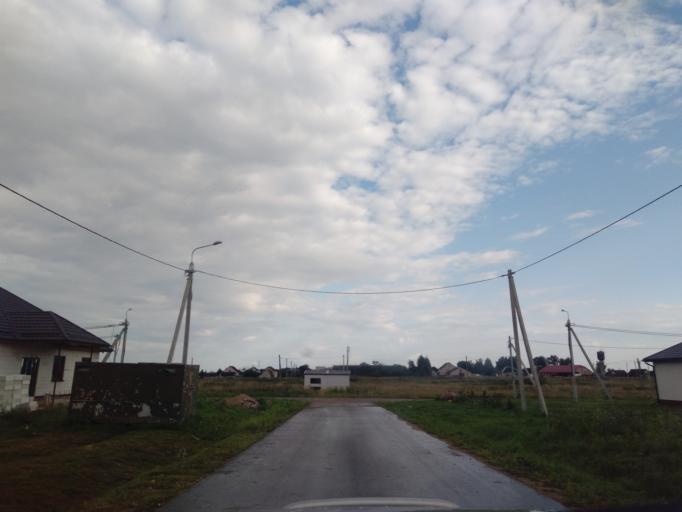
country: BY
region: Minsk
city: Kapyl'
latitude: 53.1637
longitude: 27.0783
